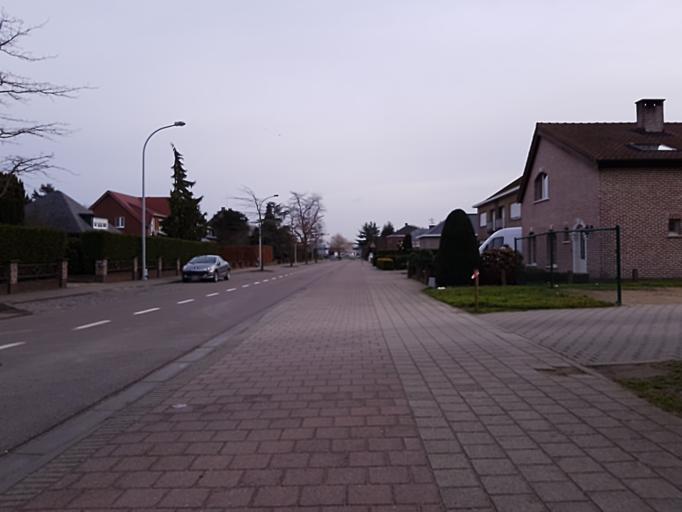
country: BE
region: Flanders
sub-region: Provincie Antwerpen
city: Putte
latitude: 51.0561
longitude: 4.6745
